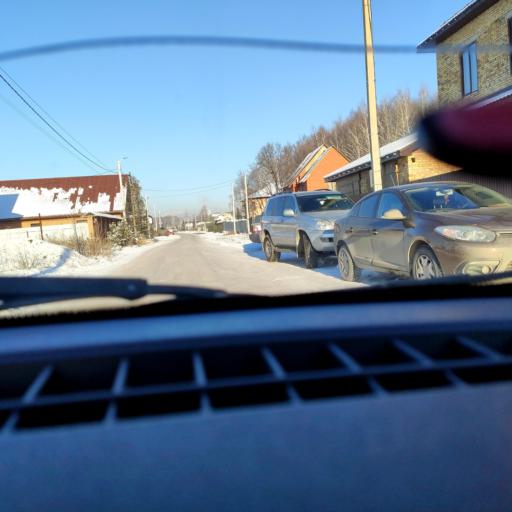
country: RU
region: Bashkortostan
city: Ufa
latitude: 54.6616
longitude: 55.9249
